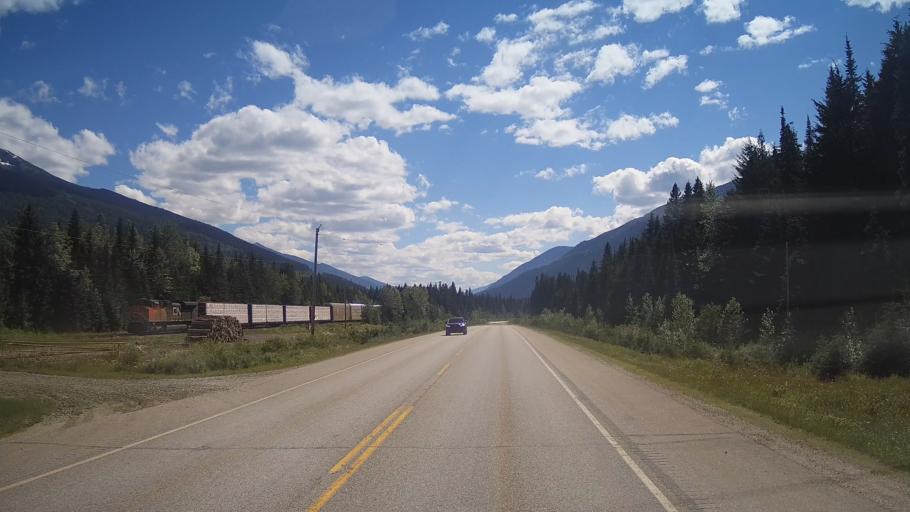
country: CA
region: Alberta
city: Jasper Park Lodge
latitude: 52.5760
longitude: -119.0980
